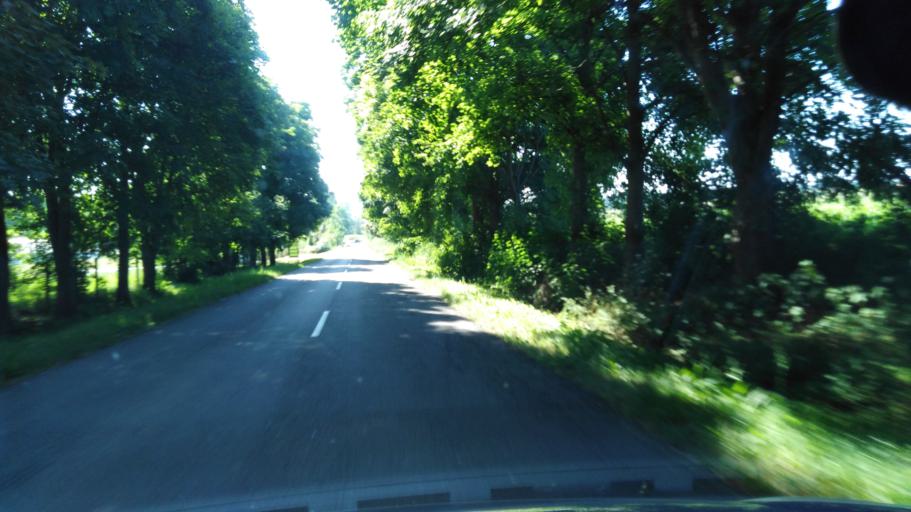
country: HU
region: Nograd
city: Retsag
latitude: 47.9332
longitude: 19.1617
